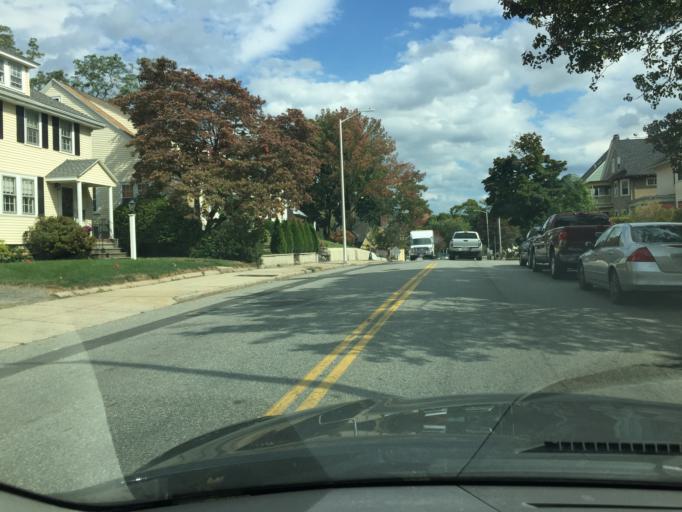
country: US
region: Massachusetts
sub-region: Middlesex County
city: Medford
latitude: 42.4218
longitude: -71.1245
